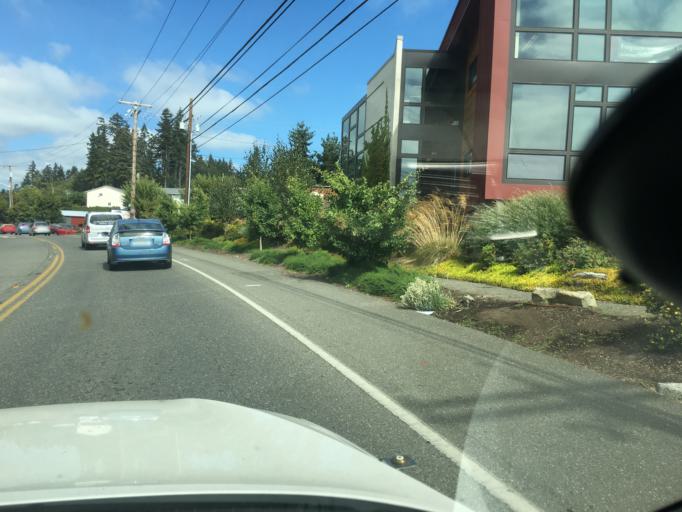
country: US
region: Washington
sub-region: Kitsap County
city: Kingston
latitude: 47.8002
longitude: -122.4986
